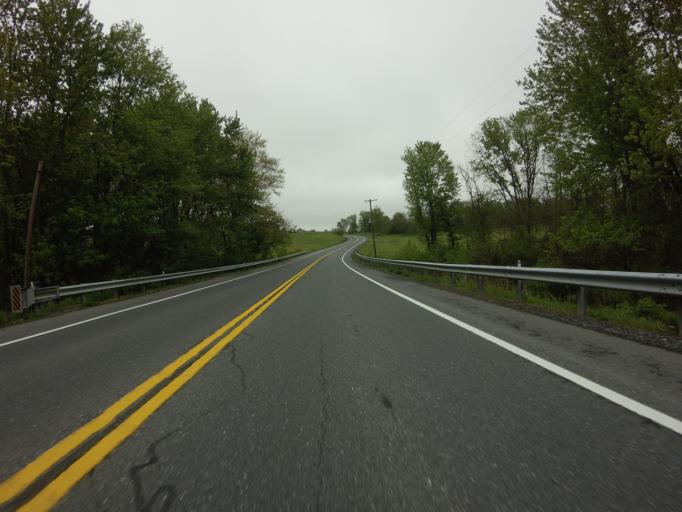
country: US
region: Maryland
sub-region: Frederick County
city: Linganore
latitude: 39.4928
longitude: -77.2037
